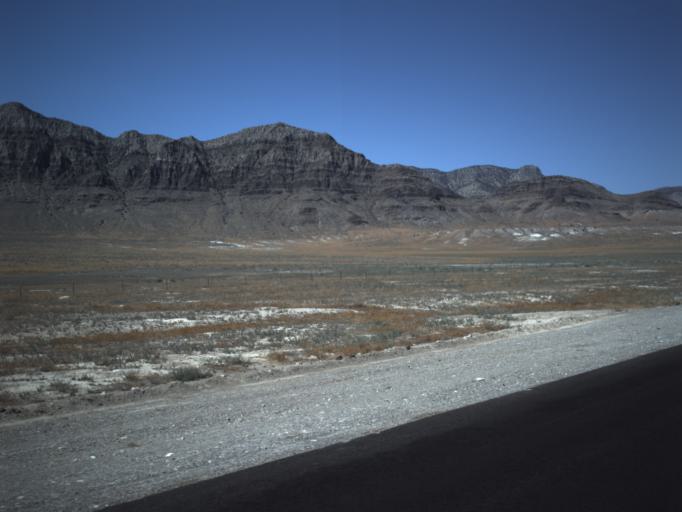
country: US
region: Utah
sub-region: Beaver County
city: Milford
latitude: 39.0771
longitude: -113.4790
